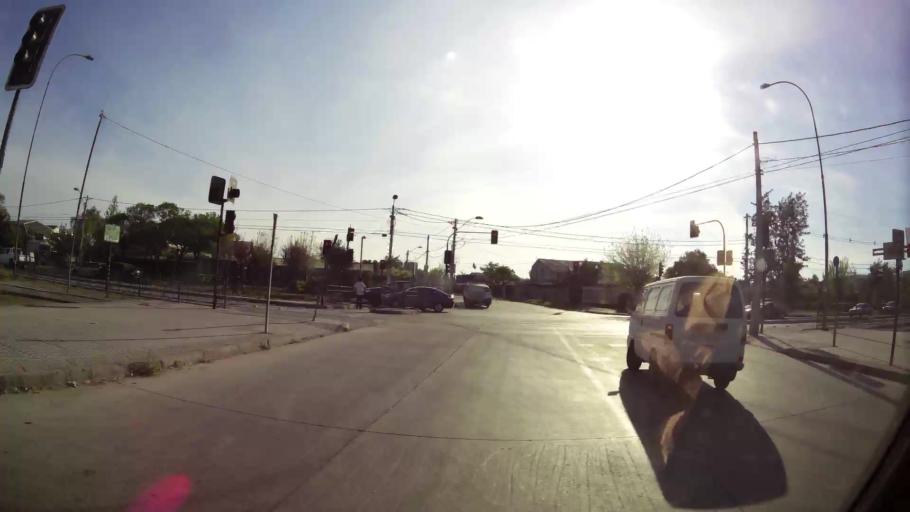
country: CL
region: Santiago Metropolitan
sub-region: Provincia de Santiago
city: Santiago
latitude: -33.5091
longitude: -70.6256
